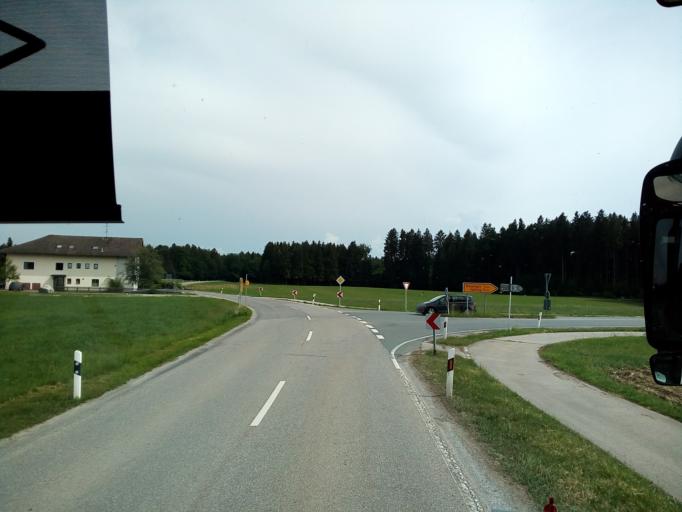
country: DE
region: Bavaria
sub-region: Upper Bavaria
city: Obing
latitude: 47.9902
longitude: 12.4197
